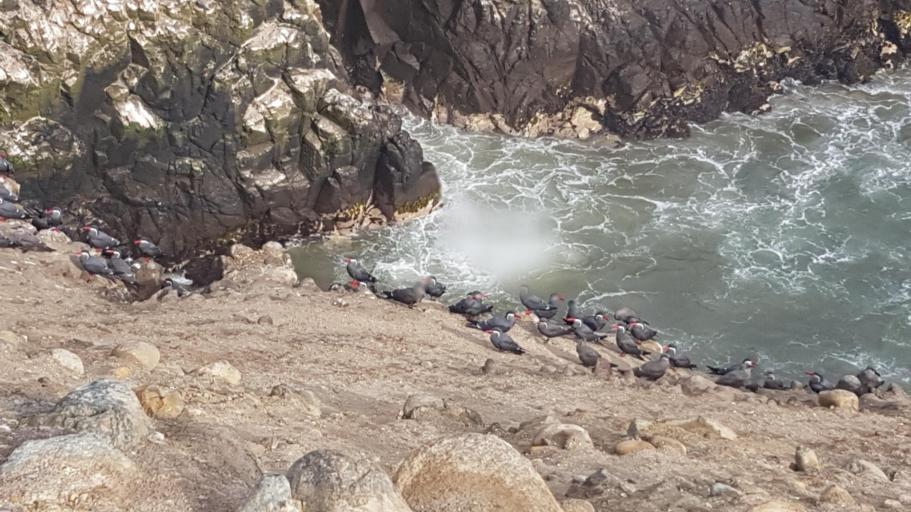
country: PE
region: Lima
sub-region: Barranca
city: Puerto Supe
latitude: -10.8003
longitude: -77.7506
